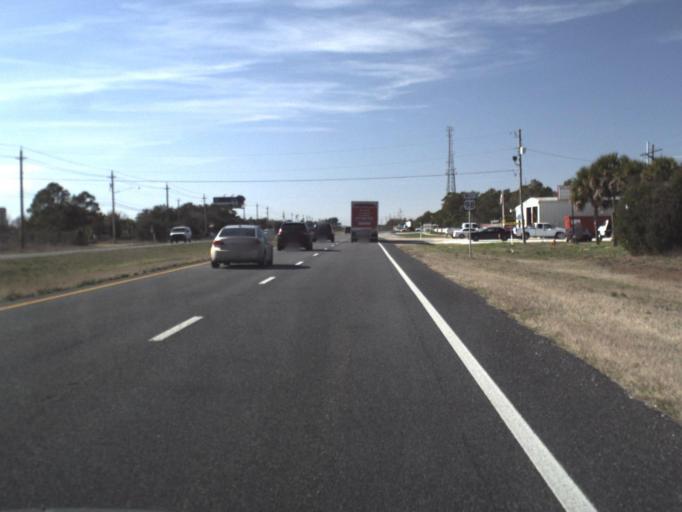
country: US
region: Florida
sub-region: Bay County
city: Laguna Beach
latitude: 30.2508
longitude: -85.9335
